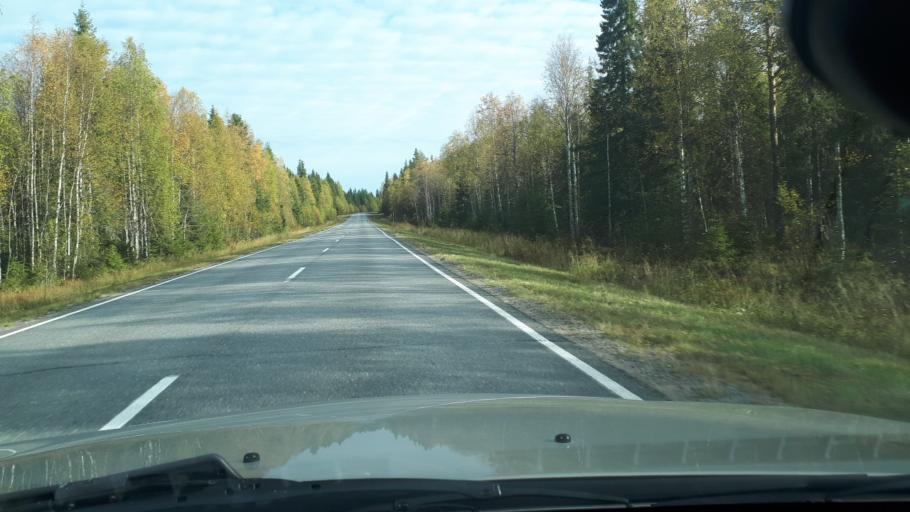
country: FI
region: Northern Ostrobothnia
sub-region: Oulu
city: Yli-Ii
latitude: 65.9477
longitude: 25.9039
